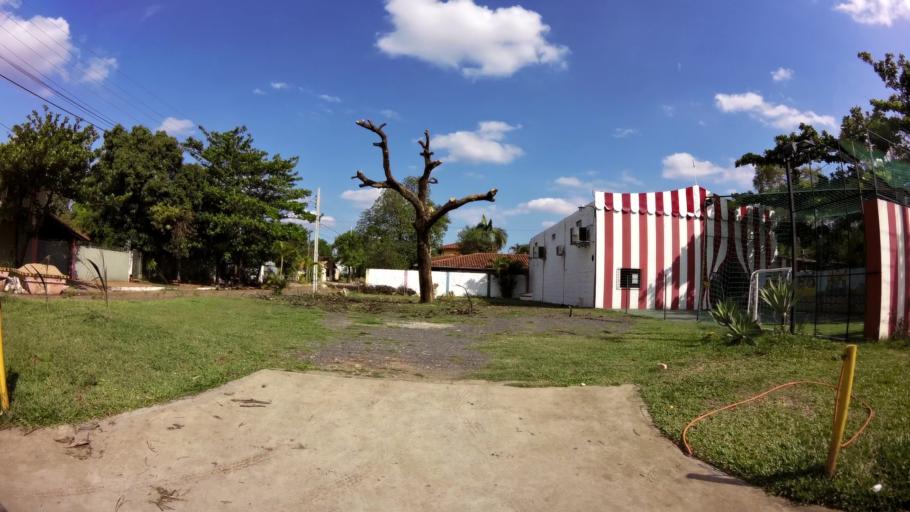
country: PY
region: Central
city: Fernando de la Mora
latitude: -25.3142
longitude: -57.5349
